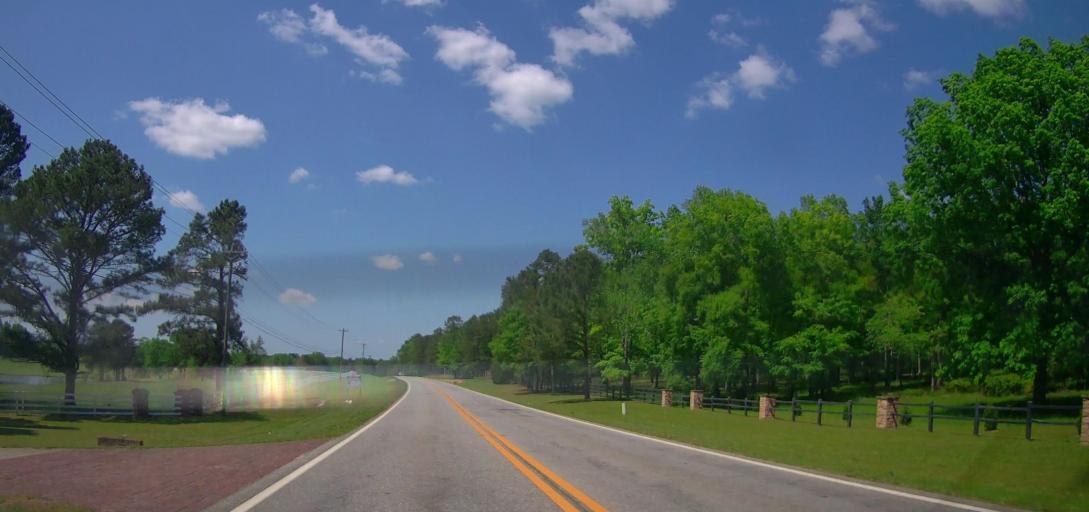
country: US
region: Georgia
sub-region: Putnam County
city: Eatonton
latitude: 33.2943
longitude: -83.3019
